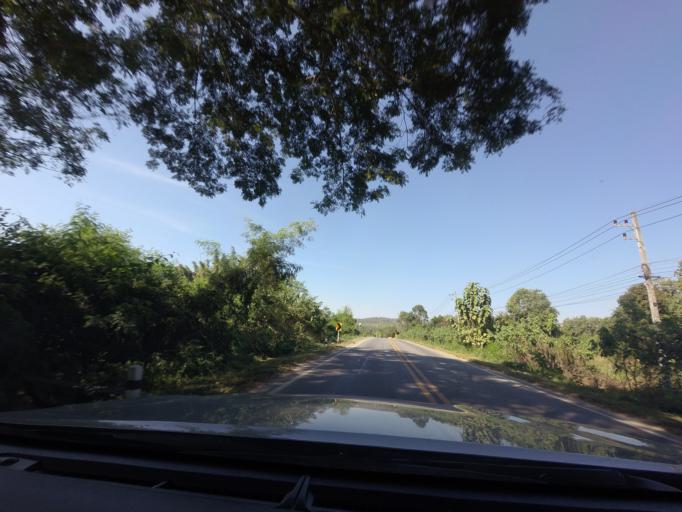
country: TH
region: Sukhothai
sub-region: Amphoe Si Satchanalai
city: Si Satchanalai
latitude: 17.6269
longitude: 99.7011
